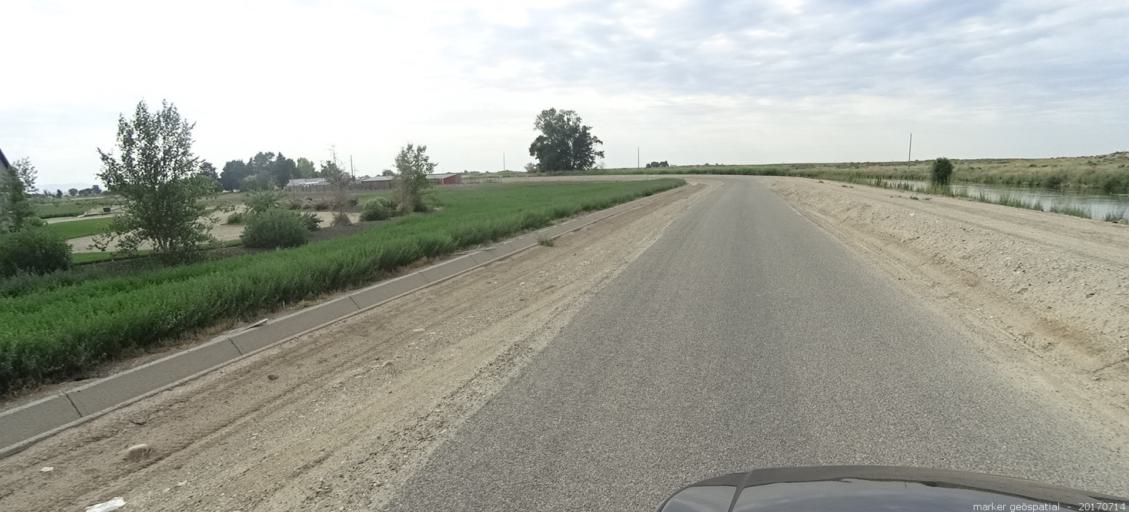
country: US
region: Idaho
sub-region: Ada County
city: Kuna
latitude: 43.4610
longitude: -116.3686
